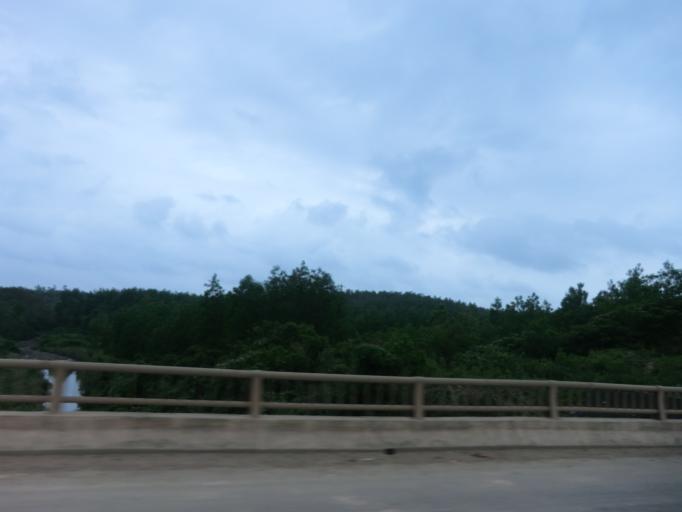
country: VN
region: Quang Tri
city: Cam Lo
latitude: 16.7990
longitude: 107.0421
